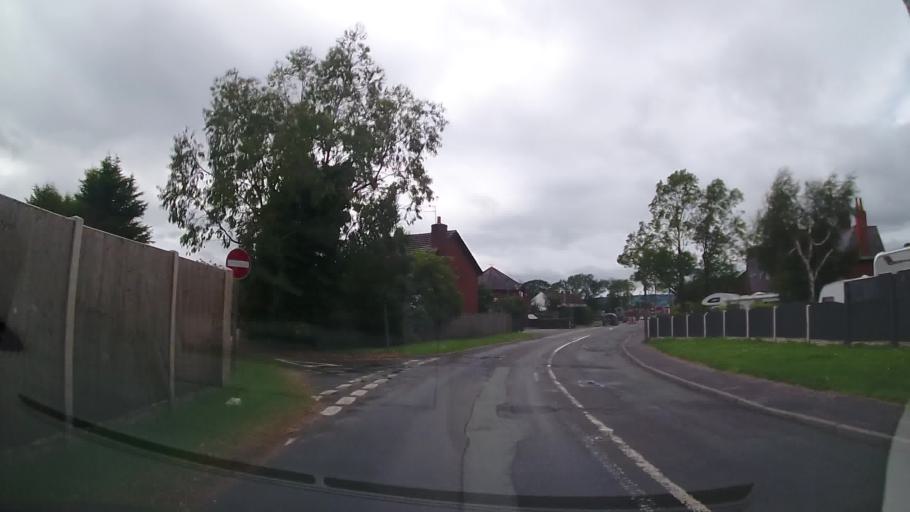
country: GB
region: England
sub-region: Shropshire
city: Gobowen
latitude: 52.9208
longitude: -3.0119
